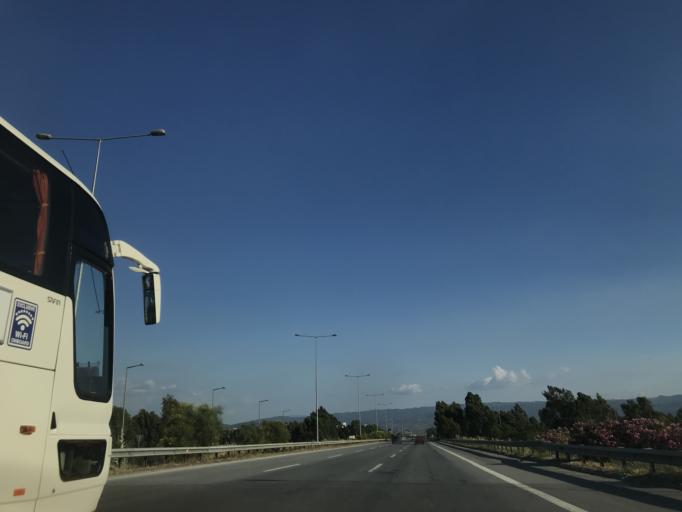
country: TR
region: Aydin
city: Aydin
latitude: 37.8476
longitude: 27.8074
